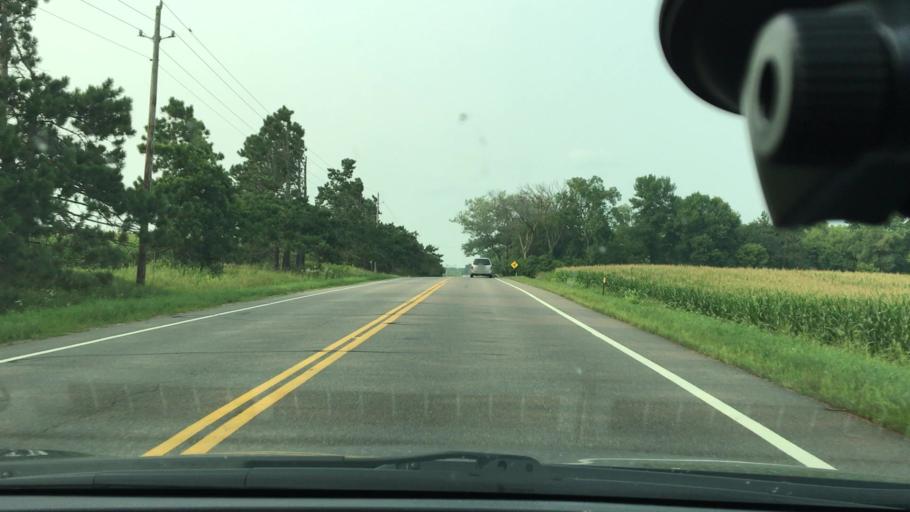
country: US
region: Minnesota
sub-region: Hennepin County
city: Champlin
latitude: 45.1780
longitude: -93.4623
